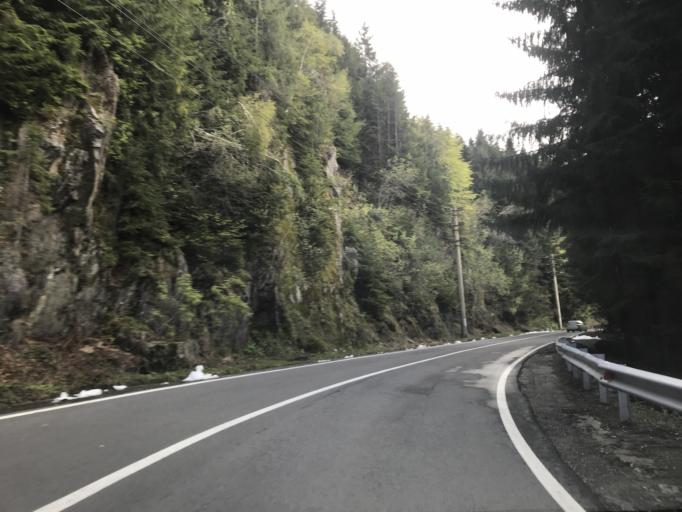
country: RO
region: Sibiu
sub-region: Comuna Cartisoara
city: Cartisoara
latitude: 45.6543
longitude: 24.6036
